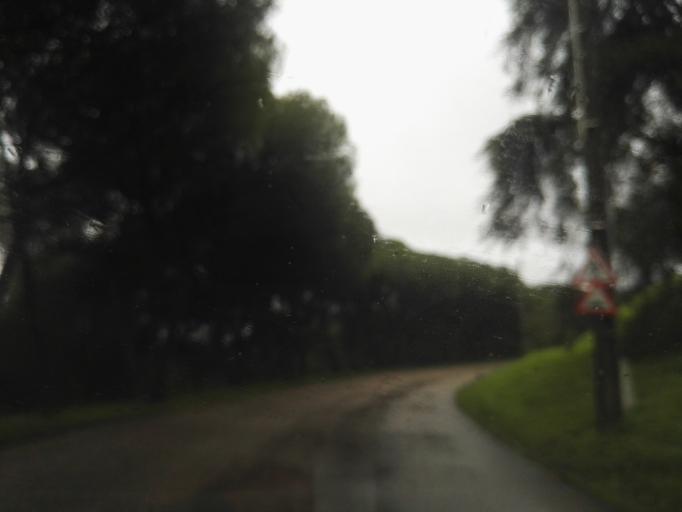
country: PT
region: Lisbon
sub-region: Odivelas
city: Pontinha
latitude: 38.7405
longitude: -9.1859
